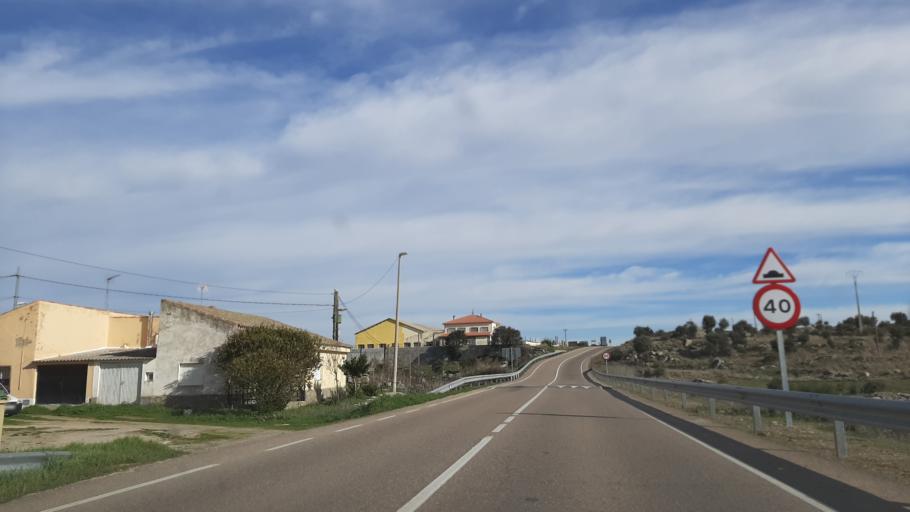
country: ES
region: Castille and Leon
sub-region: Provincia de Salamanca
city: Ledesma
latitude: 41.0922
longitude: -5.9931
